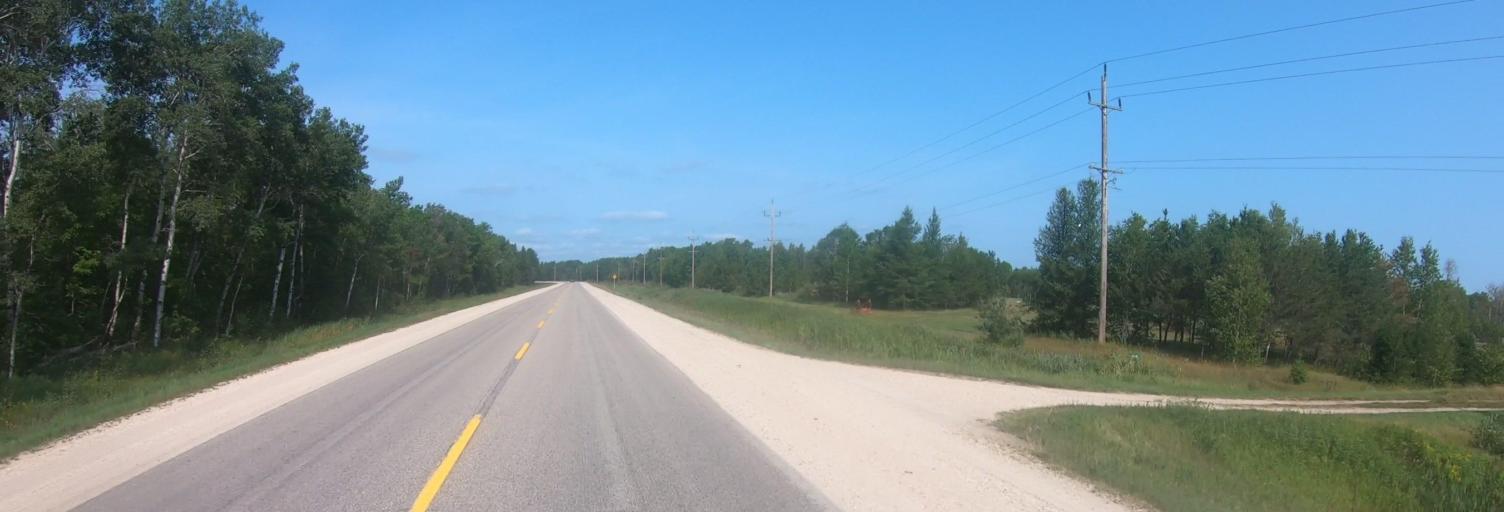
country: CA
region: Manitoba
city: La Broquerie
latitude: 49.1709
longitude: -96.1562
